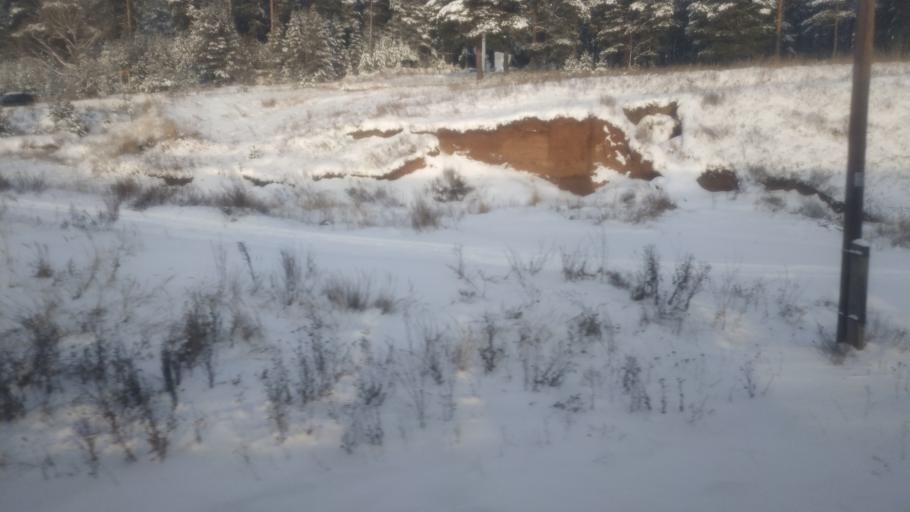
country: RU
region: Kirov
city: Krasnaya Polyana
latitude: 56.2471
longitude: 51.1628
